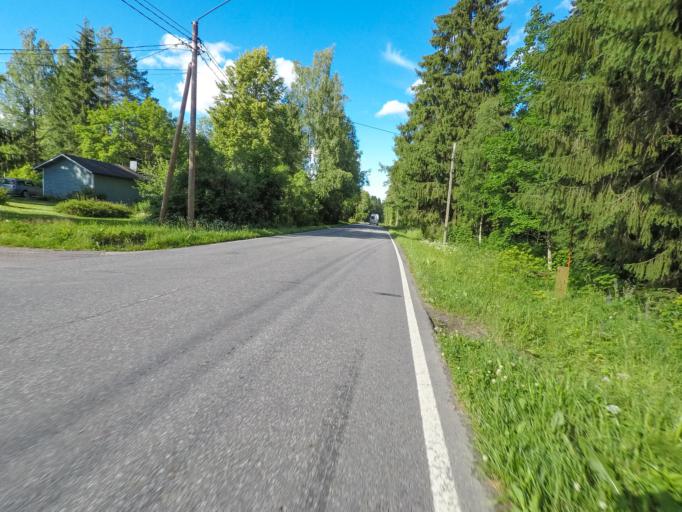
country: FI
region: South Karelia
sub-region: Imatra
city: Imatra
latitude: 61.1444
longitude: 28.7468
